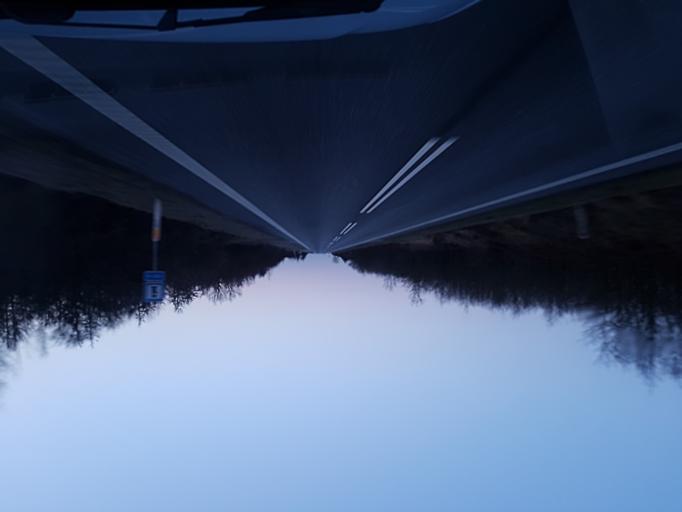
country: DK
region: Central Jutland
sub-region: Holstebro Kommune
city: Holstebro
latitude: 56.2255
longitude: 8.5987
